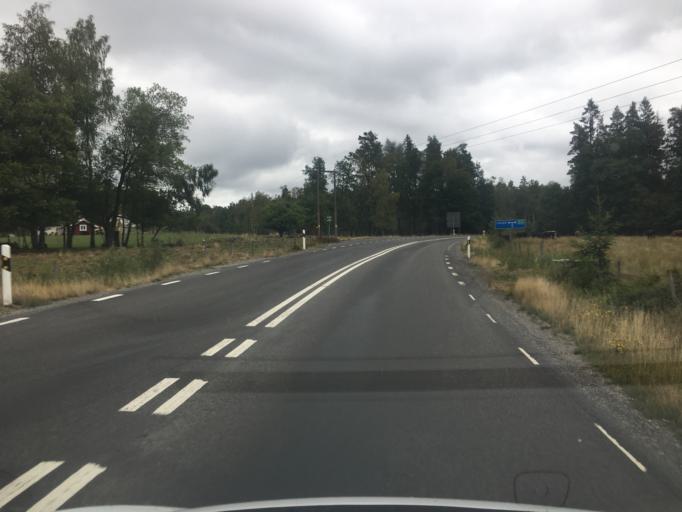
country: SE
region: Kronoberg
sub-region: Ljungby Kommun
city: Lagan
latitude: 57.0411
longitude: 14.0397
